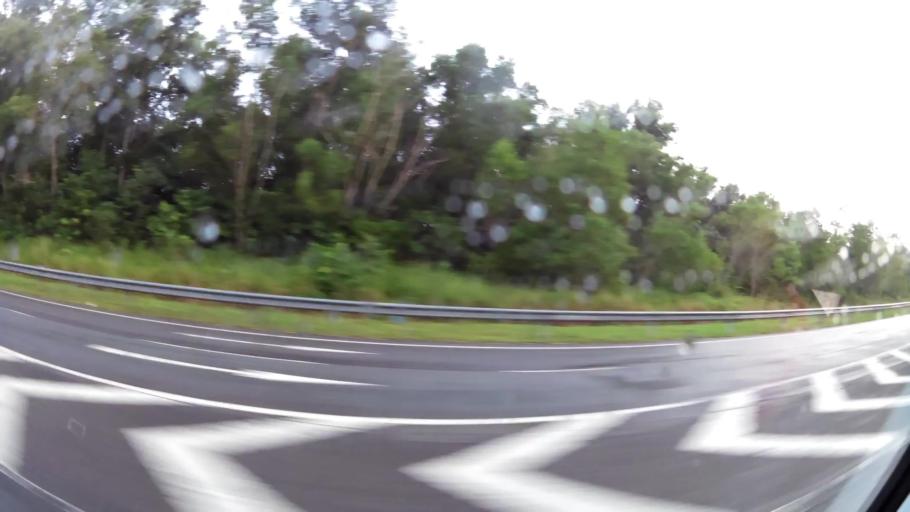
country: BN
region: Brunei and Muara
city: Bandar Seri Begawan
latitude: 4.9265
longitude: 114.9644
